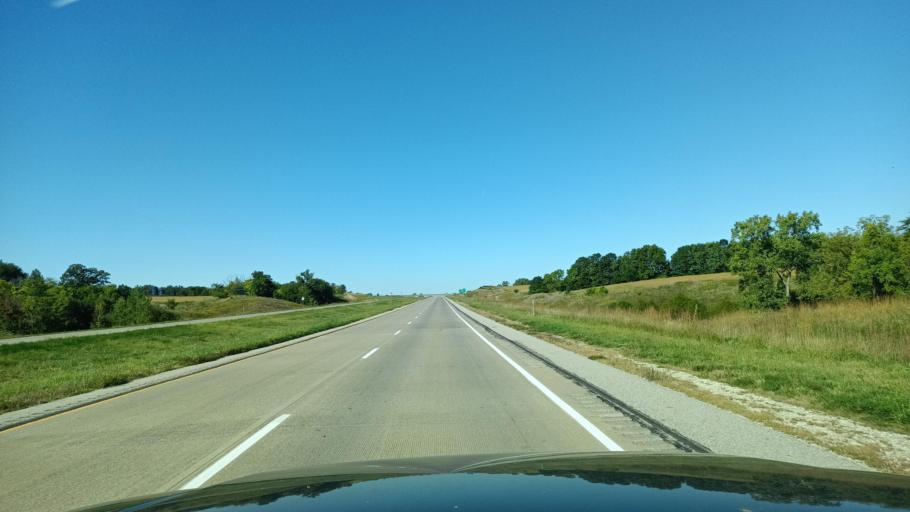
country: US
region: Iowa
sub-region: Lee County
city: Fort Madison
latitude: 40.6707
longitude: -91.3142
